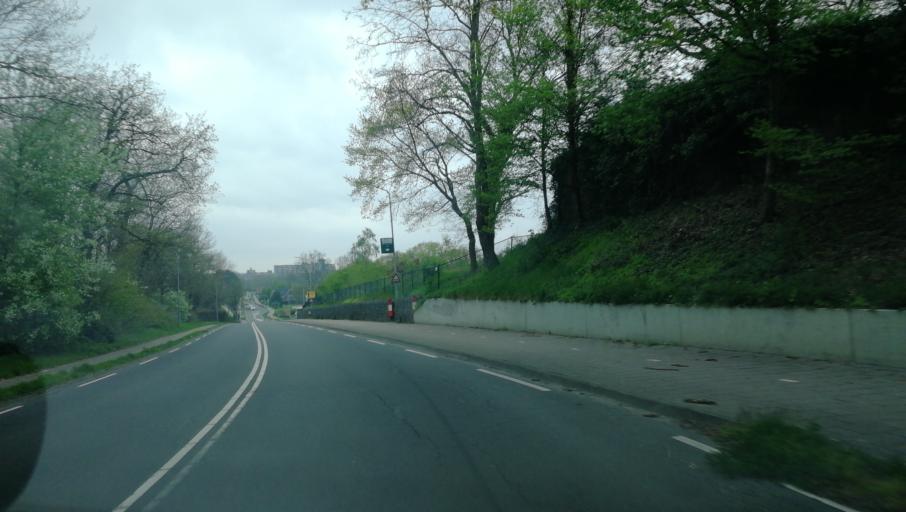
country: NL
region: Limburg
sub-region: Gemeente Venlo
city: Venlo
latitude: 51.3756
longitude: 6.2042
